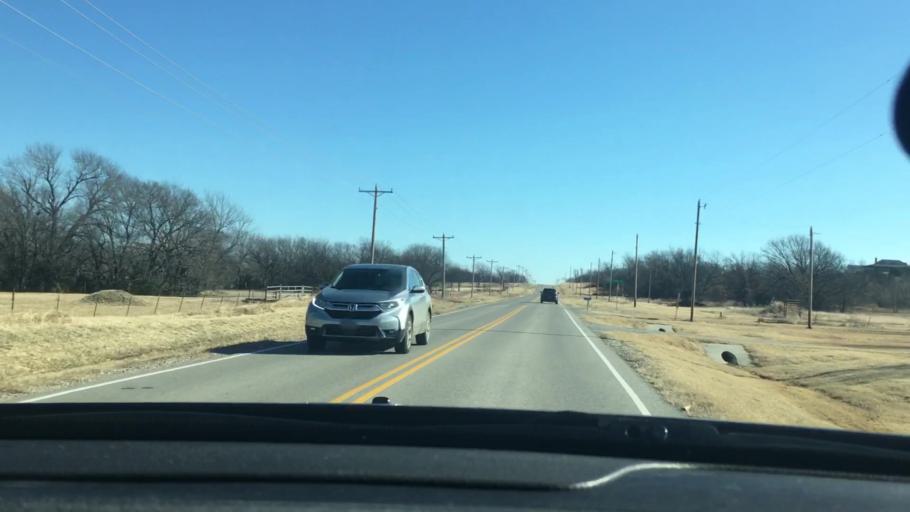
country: US
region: Oklahoma
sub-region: Murray County
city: Davis
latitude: 34.4774
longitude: -97.1266
